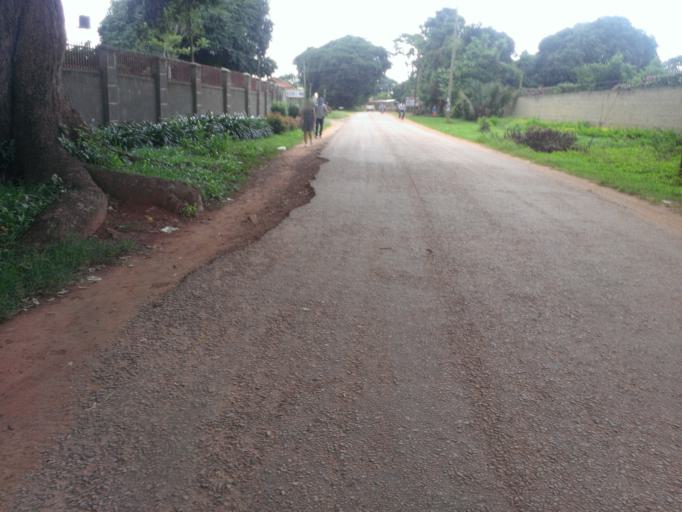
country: UG
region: Northern Region
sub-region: Gulu District
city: Gulu
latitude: 2.7821
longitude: 32.2987
